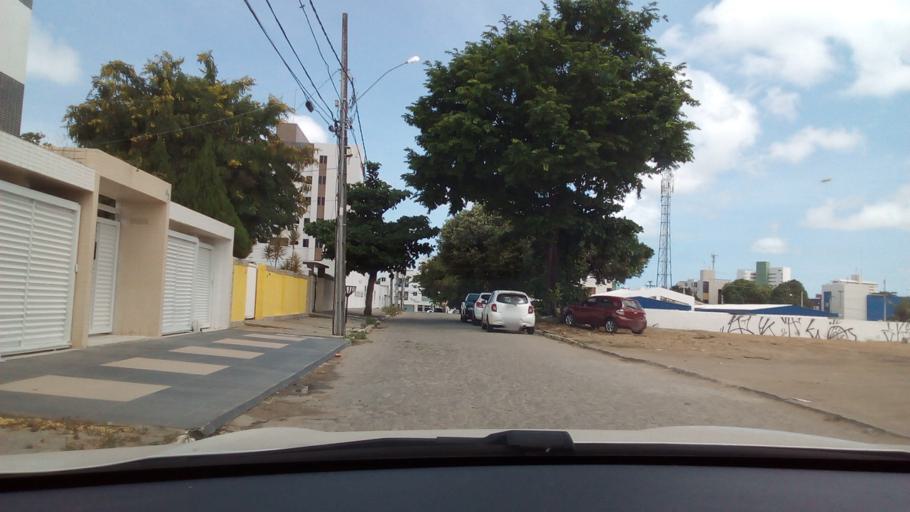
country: BR
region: Paraiba
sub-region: Joao Pessoa
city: Joao Pessoa
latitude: -7.1479
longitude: -34.8425
